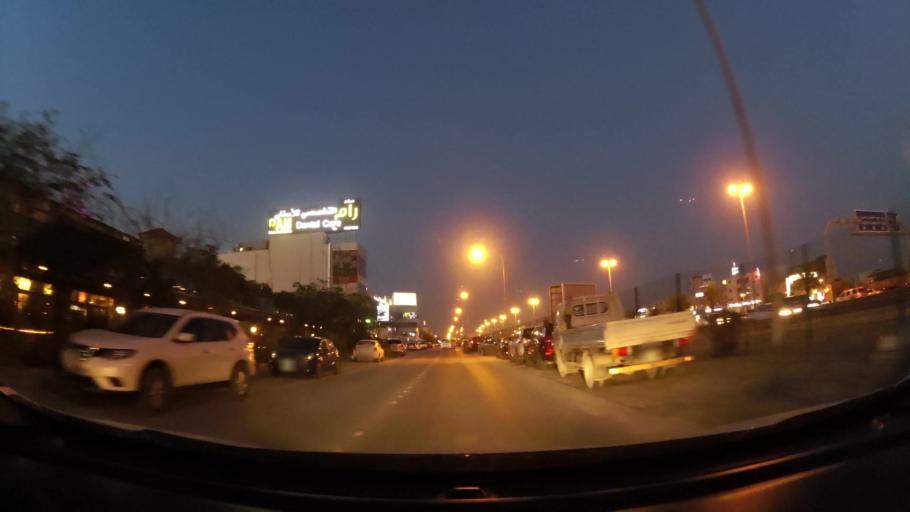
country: BH
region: Manama
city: Jidd Hafs
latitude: 26.2002
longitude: 50.5577
